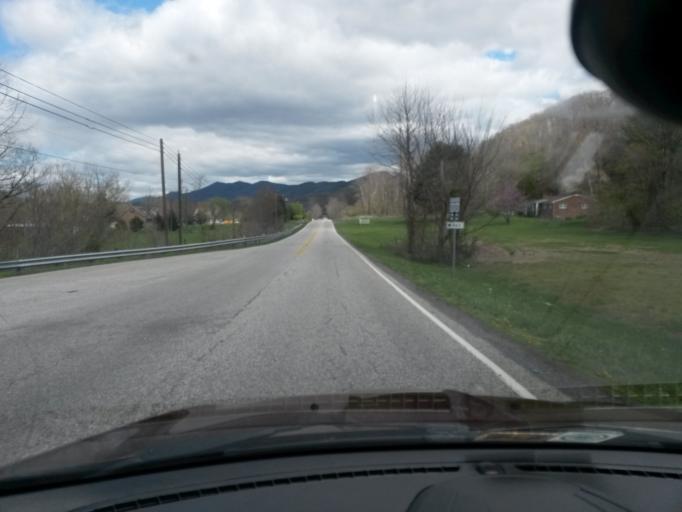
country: US
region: Virginia
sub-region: City of Buena Vista
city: Buena Vista
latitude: 37.7026
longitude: -79.3842
